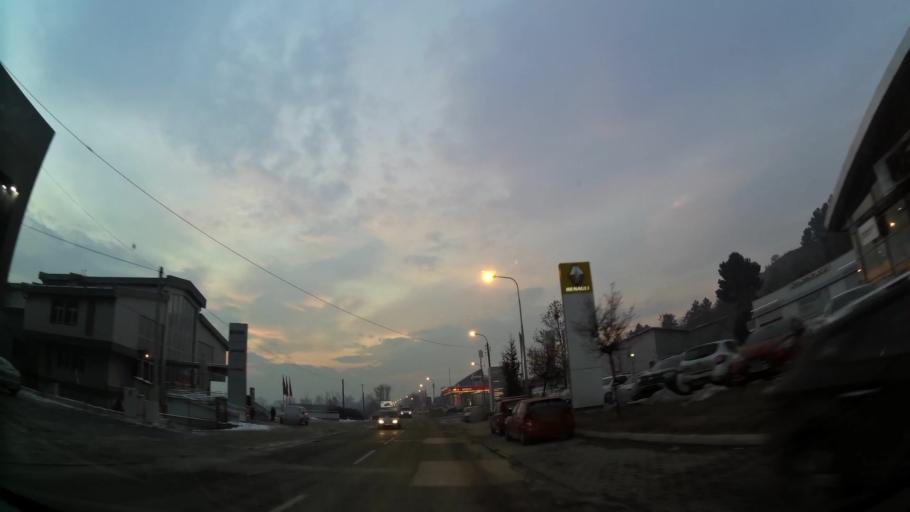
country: MK
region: Suto Orizari
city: Suto Orizare
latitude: 42.0150
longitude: 21.4010
